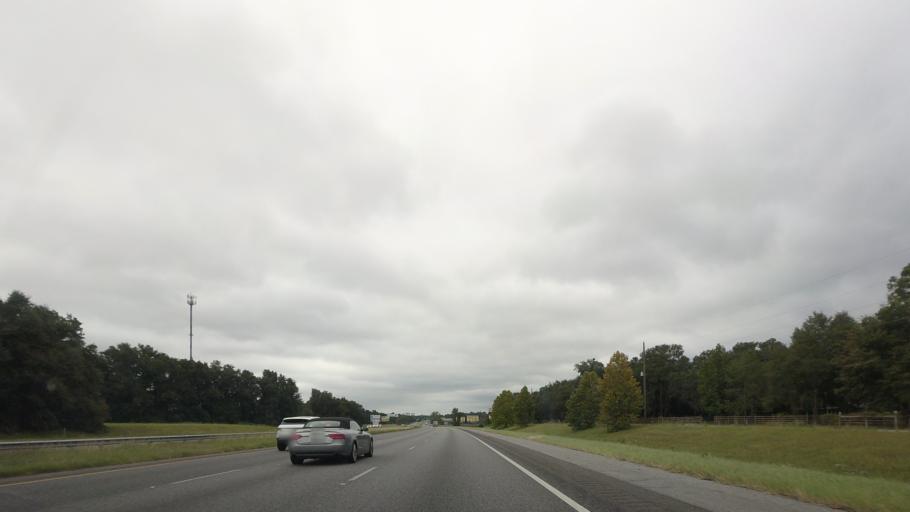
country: US
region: Georgia
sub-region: Echols County
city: Statenville
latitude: 30.6611
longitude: -83.2065
